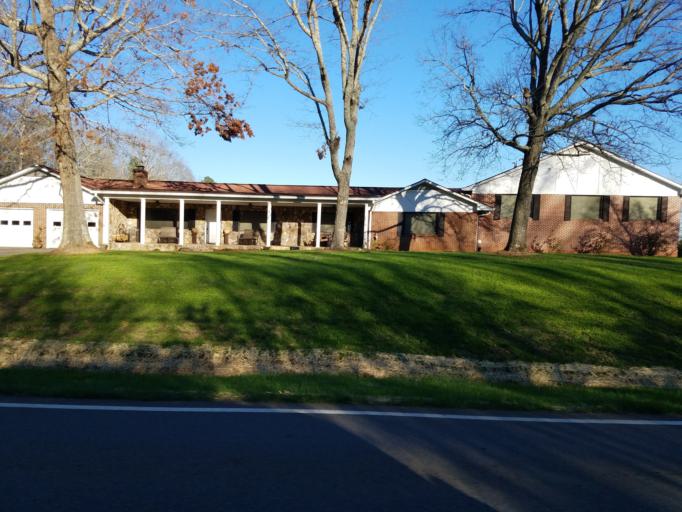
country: US
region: Georgia
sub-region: Pickens County
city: Jasper
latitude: 34.4172
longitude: -84.4200
